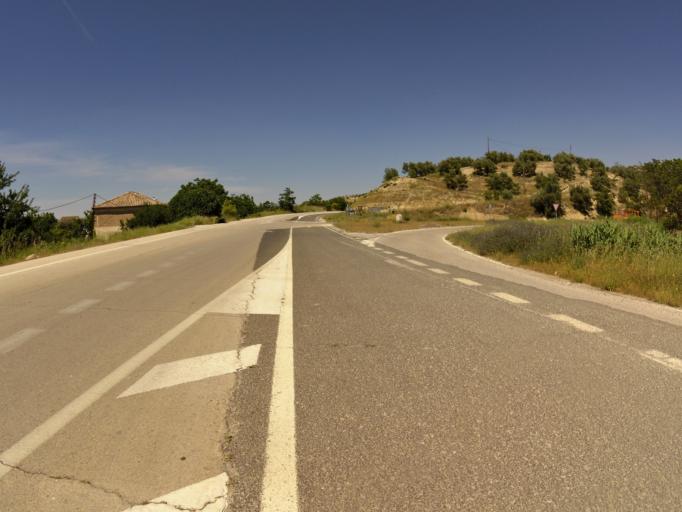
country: ES
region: Andalusia
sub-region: Provincia de Granada
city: Salar
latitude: 37.1690
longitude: -4.0874
